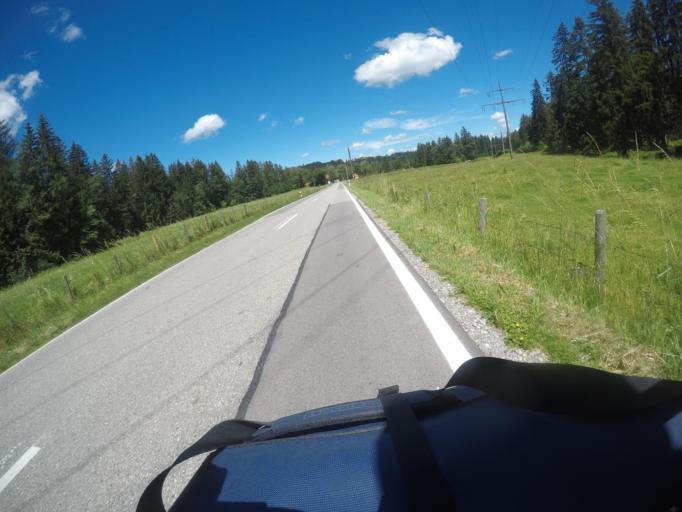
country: DE
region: Bavaria
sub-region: Upper Bavaria
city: Prem
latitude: 47.6586
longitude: 10.7860
